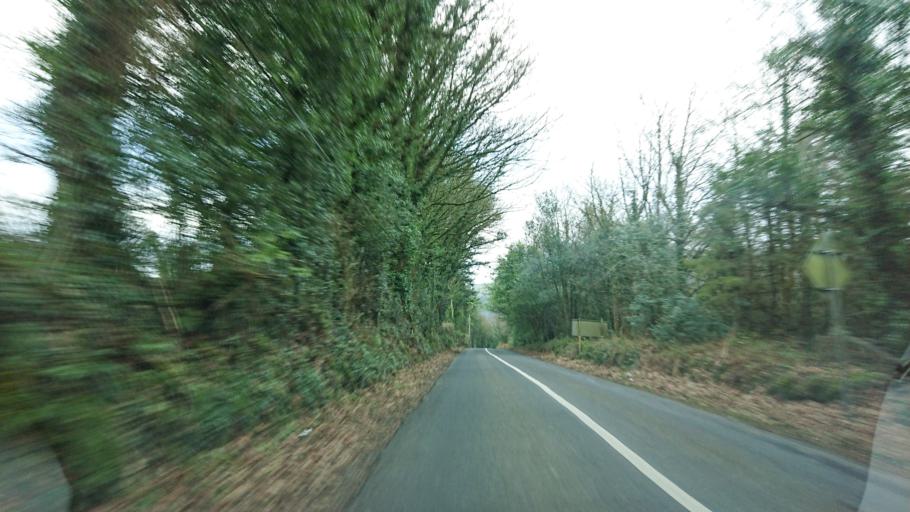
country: IE
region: Munster
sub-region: South Tipperary
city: Cluain Meala
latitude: 52.3211
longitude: -7.5785
